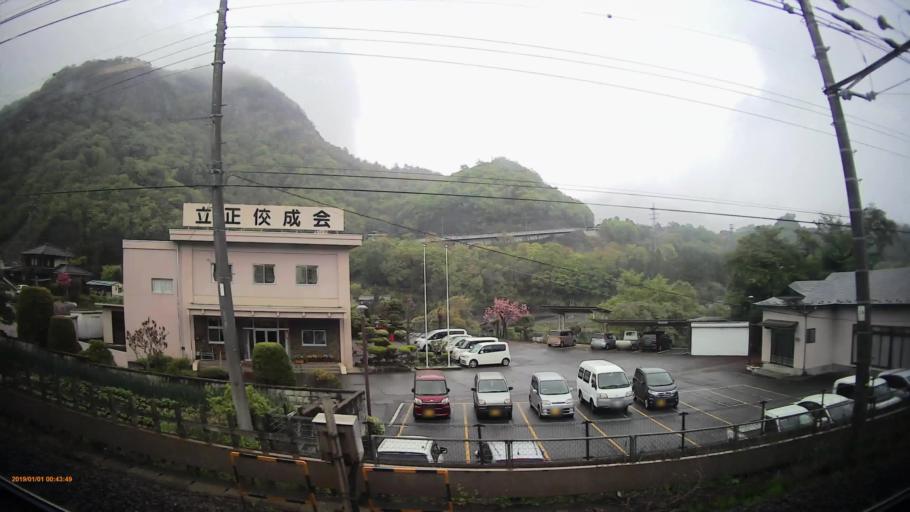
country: JP
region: Yamanashi
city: Otsuki
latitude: 35.6152
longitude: 138.9503
